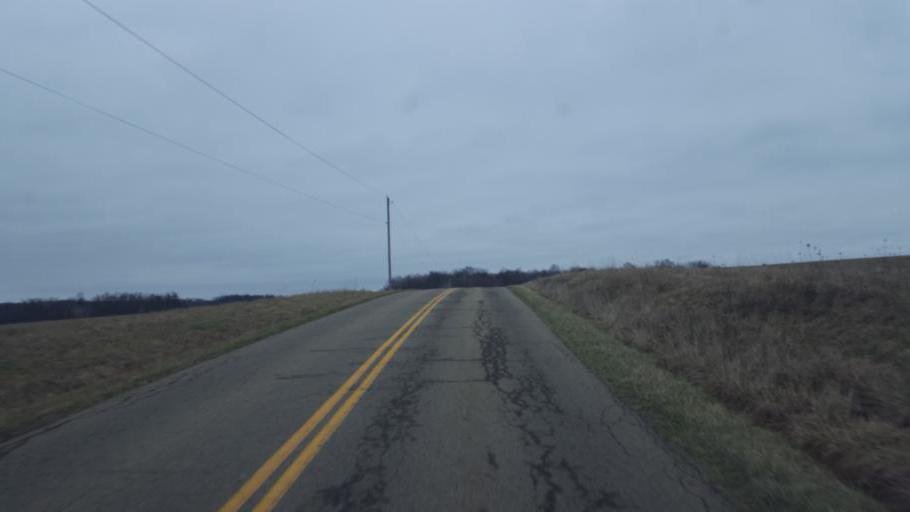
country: US
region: Ohio
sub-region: Knox County
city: Gambier
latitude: 40.4775
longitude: -82.3807
